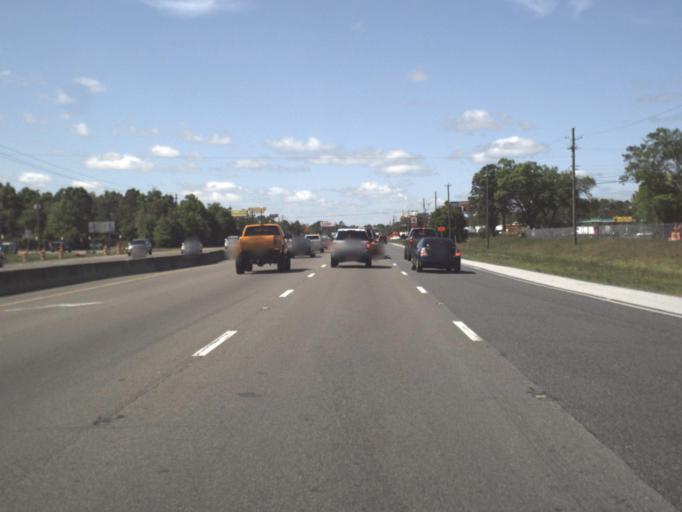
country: US
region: Florida
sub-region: Escambia County
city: Ensley
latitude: 30.5076
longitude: -87.2682
